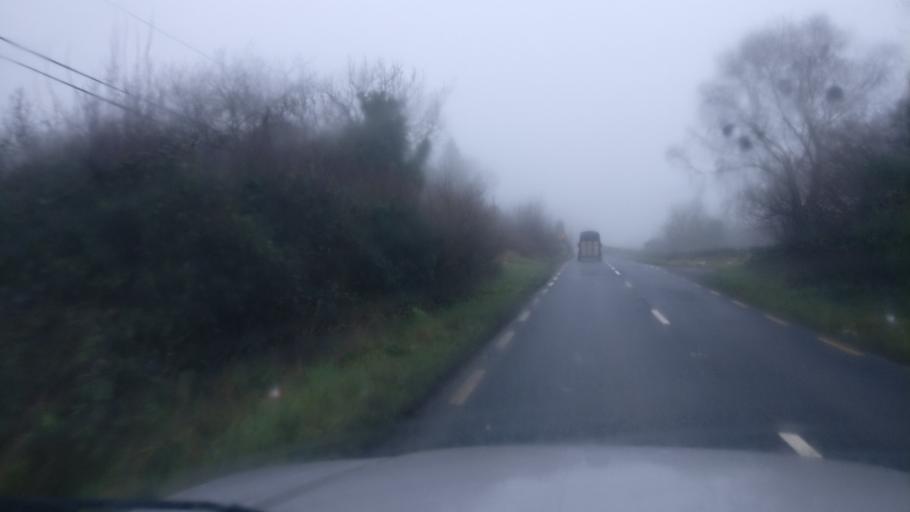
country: IE
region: Connaught
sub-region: County Galway
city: Loughrea
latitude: 53.1685
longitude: -8.6717
